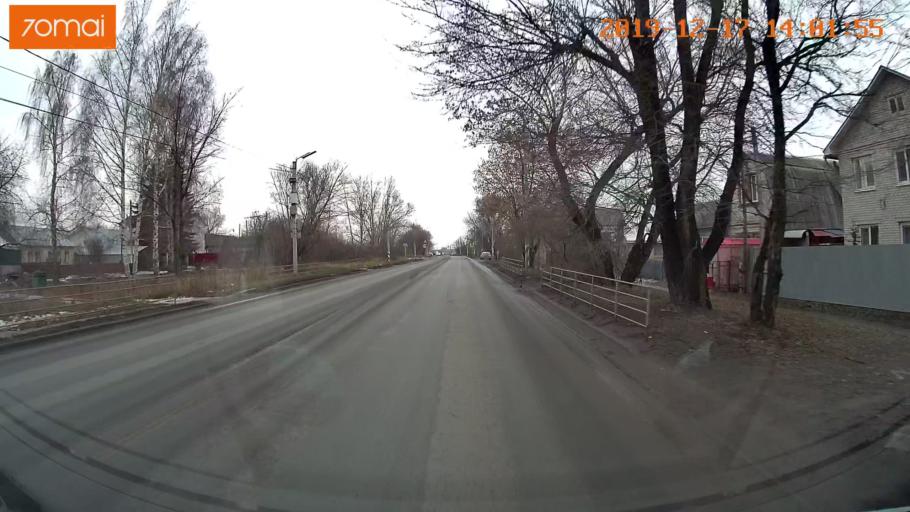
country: RU
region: Rjazan
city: Ryazan'
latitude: 54.6172
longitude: 39.6524
